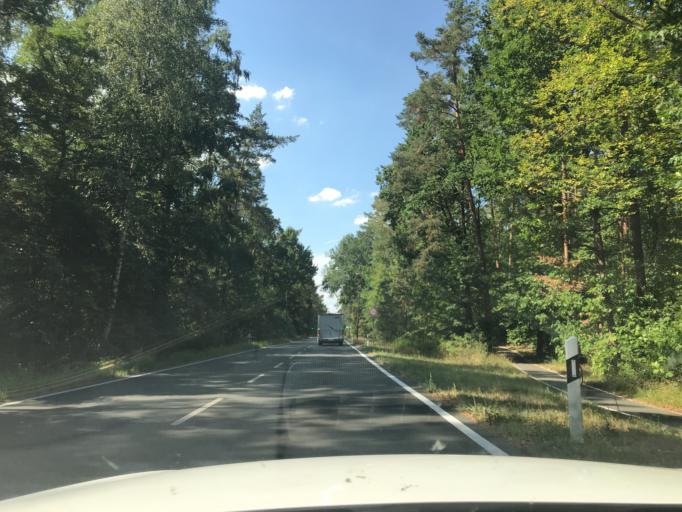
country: DE
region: Bavaria
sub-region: Regierungsbezirk Mittelfranken
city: Erlangen
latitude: 49.5600
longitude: 11.0134
